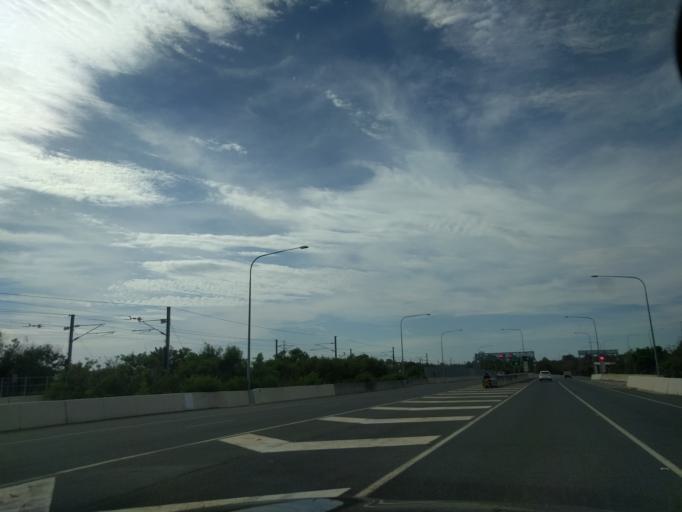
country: AU
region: Queensland
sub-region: Brisbane
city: Wacol
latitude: -27.5752
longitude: 152.9449
